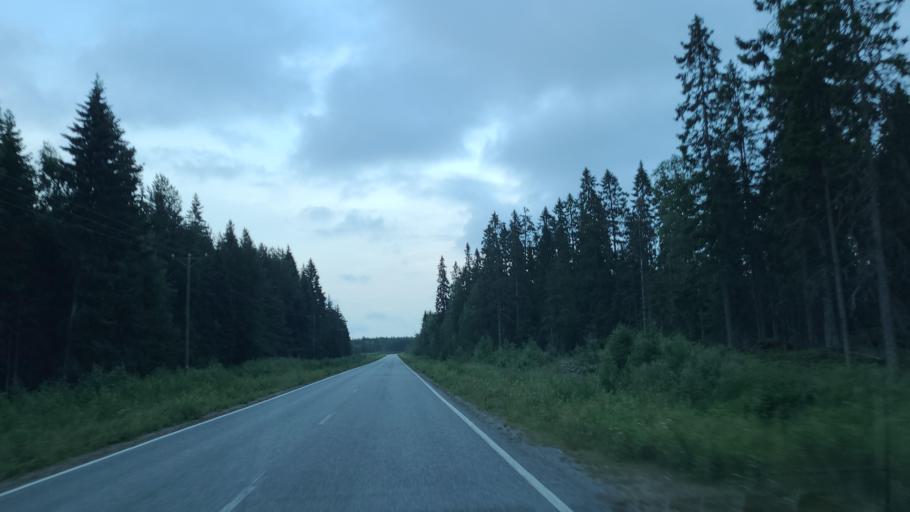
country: FI
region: Ostrobothnia
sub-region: Vaasa
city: Replot
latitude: 63.2251
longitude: 21.2335
